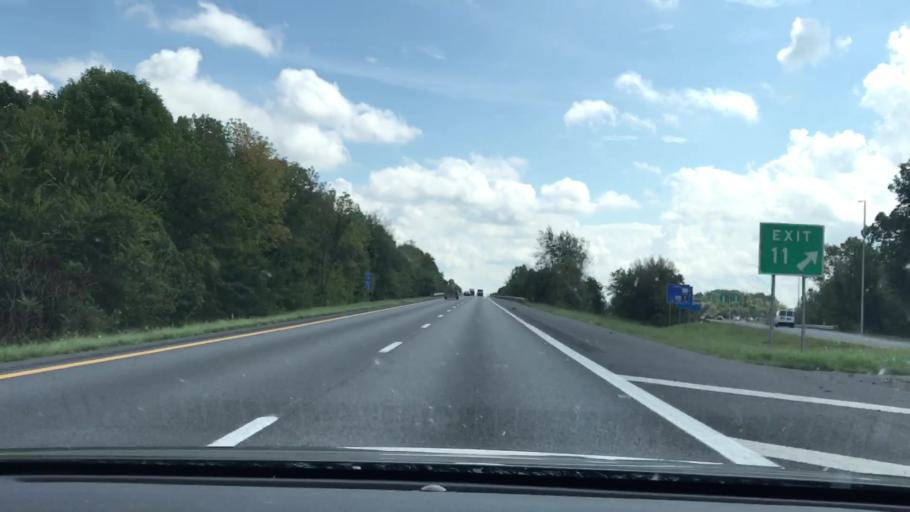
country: US
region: Tennessee
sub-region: Montgomery County
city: Clarksville
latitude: 36.5282
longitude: -87.2257
